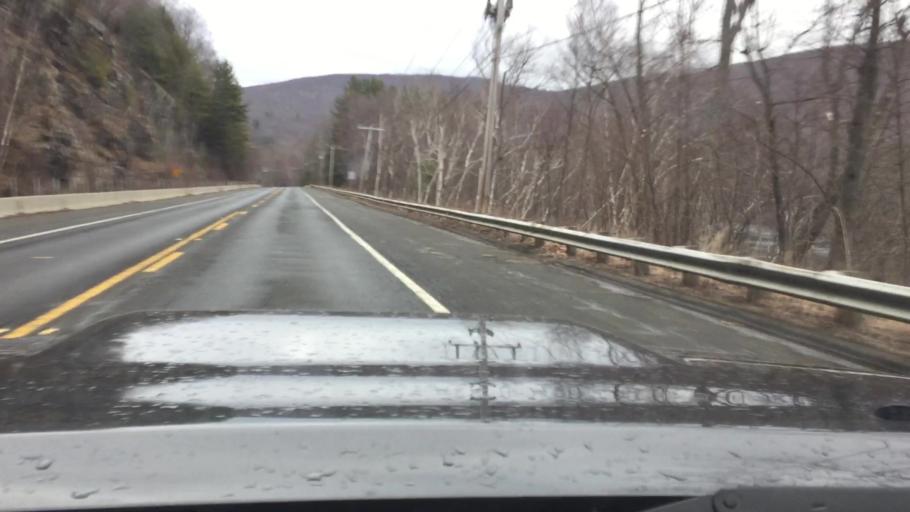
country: US
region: Massachusetts
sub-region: Hampden County
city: Westfield
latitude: 42.1668
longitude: -72.8320
